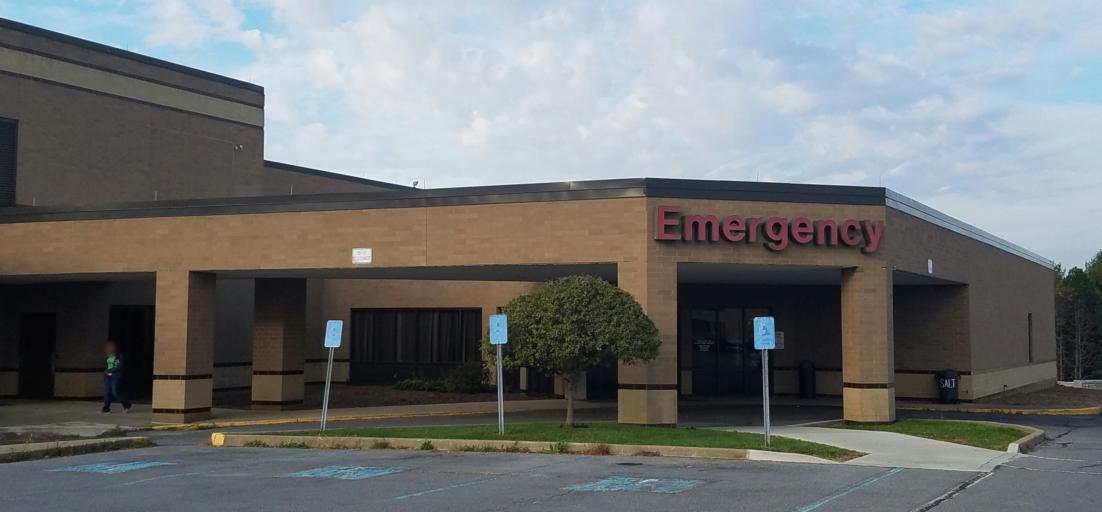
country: US
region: Pennsylvania
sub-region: Clarion County
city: Clarion
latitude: 41.1926
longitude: -79.3974
